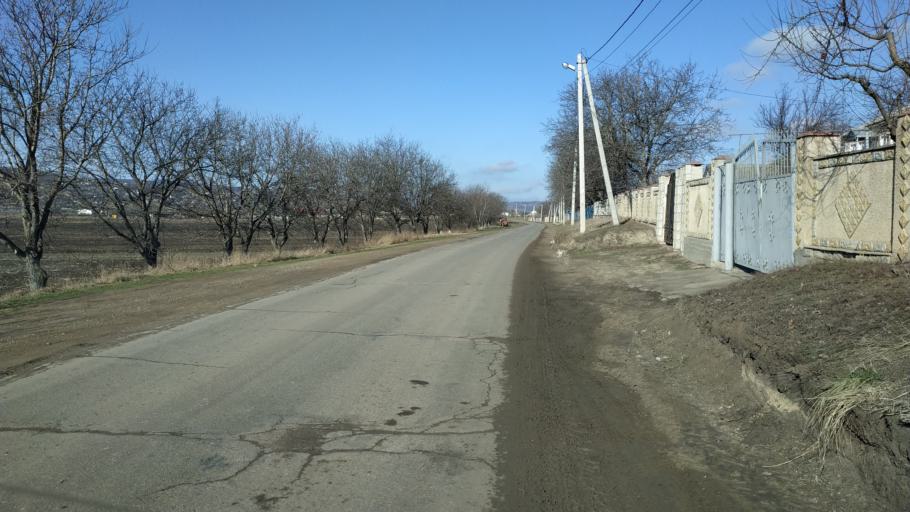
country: MD
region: Laloveni
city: Ialoveni
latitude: 46.9311
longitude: 28.6668
